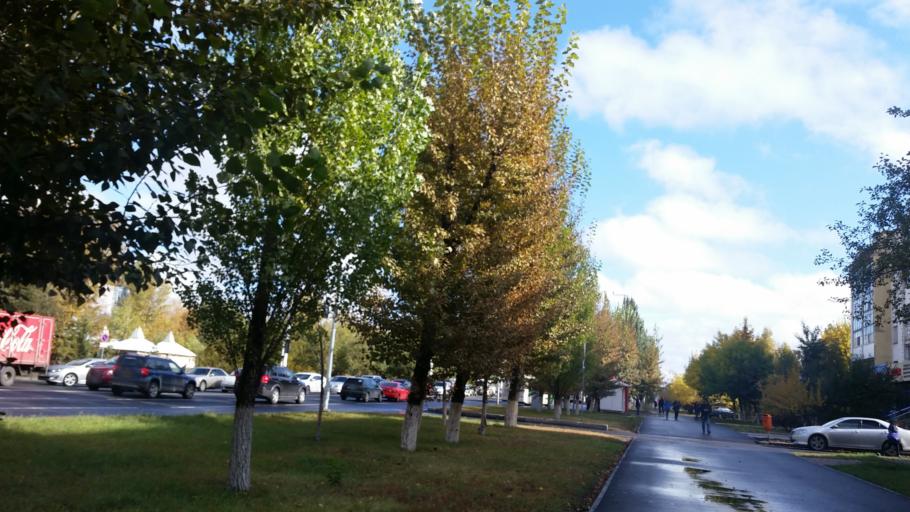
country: KZ
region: Astana Qalasy
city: Astana
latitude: 51.1587
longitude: 71.4745
